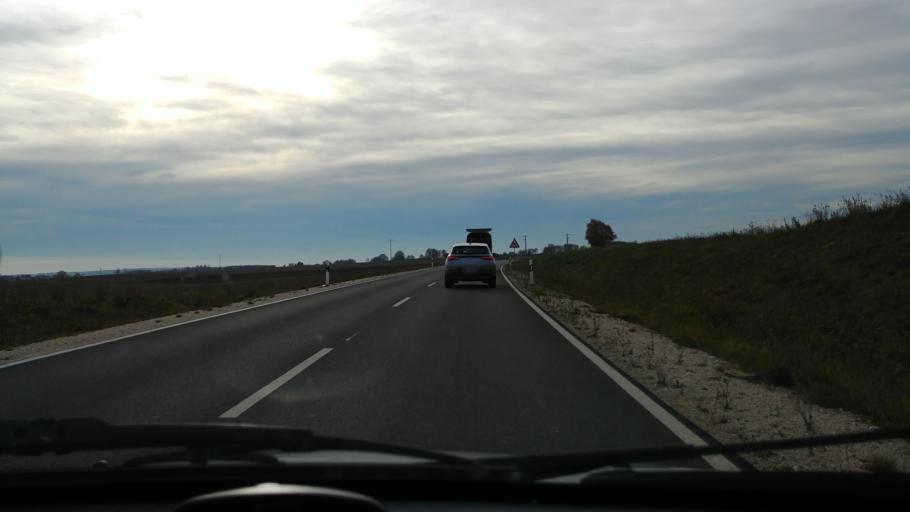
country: DE
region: Bavaria
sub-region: Swabia
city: Zoschingen
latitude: 48.6529
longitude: 10.3375
